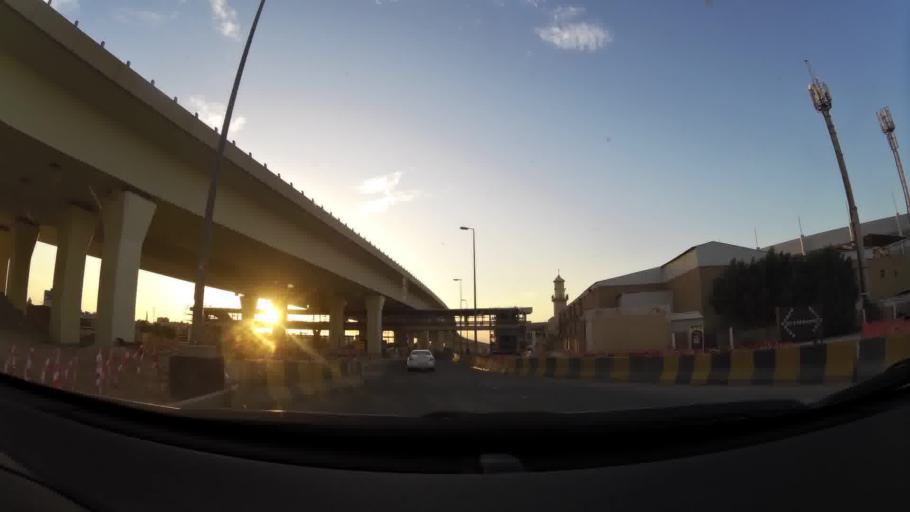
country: KW
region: Al Asimah
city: Ar Rabiyah
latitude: 29.3202
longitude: 47.8295
